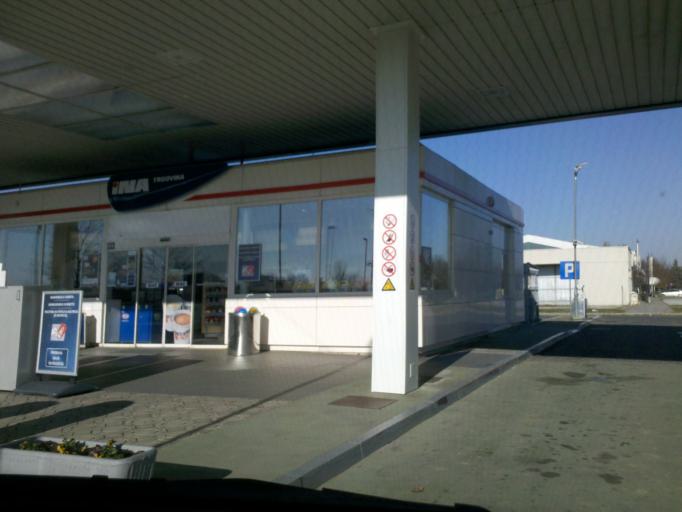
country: HR
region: Medimurska
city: Gorican
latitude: 46.4149
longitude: 16.6888
